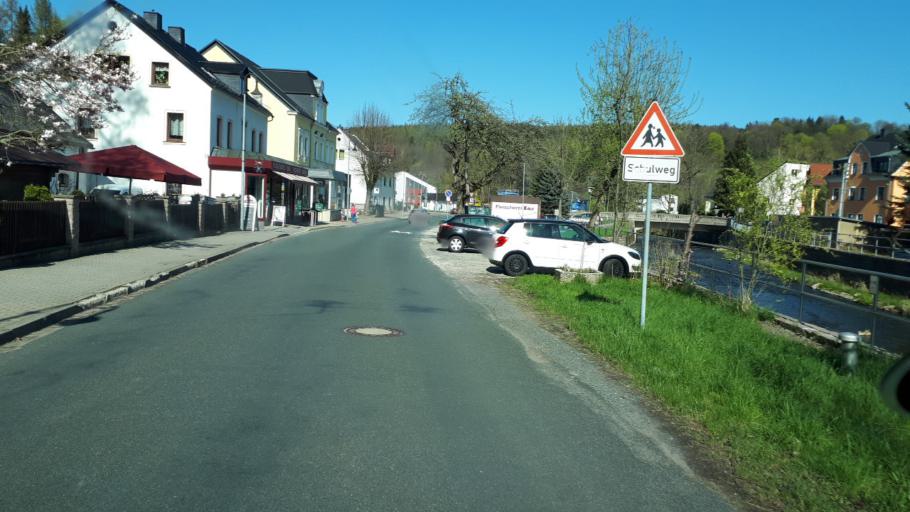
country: DE
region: Saxony
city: Gelenau
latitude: 50.7693
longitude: 12.9715
